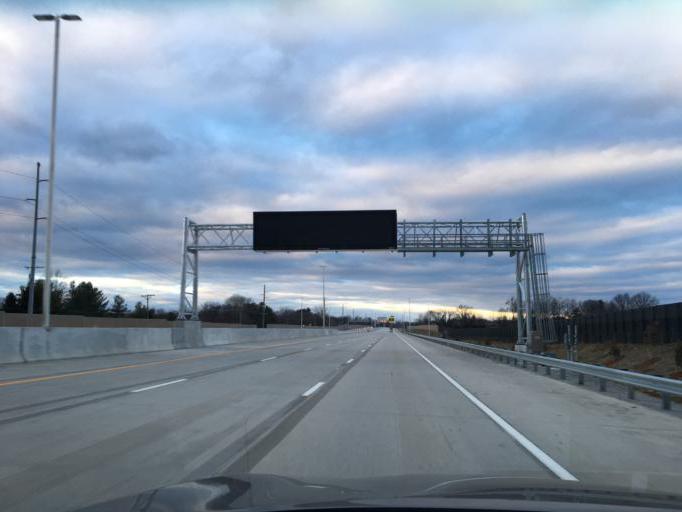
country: US
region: Kentucky
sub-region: Jefferson County
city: Barbourmeade
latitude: 38.3182
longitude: -85.5992
